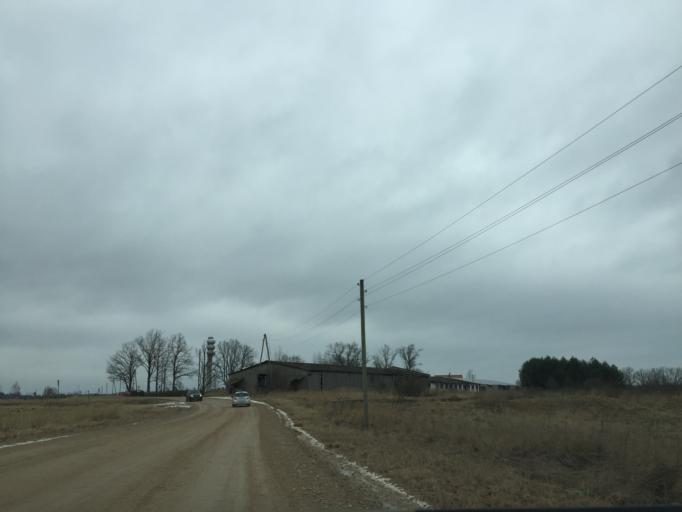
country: LV
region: Kegums
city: Kegums
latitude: 56.7622
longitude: 24.7727
